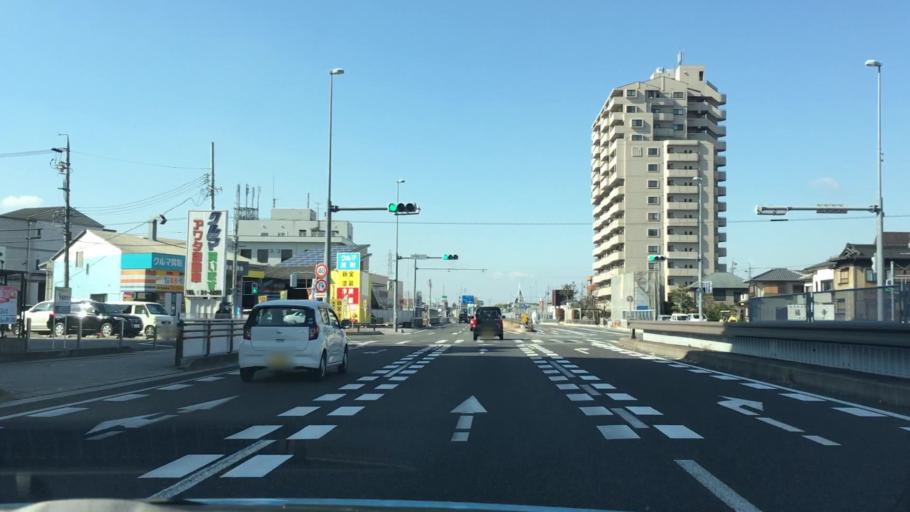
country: JP
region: Aichi
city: Okazaki
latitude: 34.9637
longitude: 137.1394
